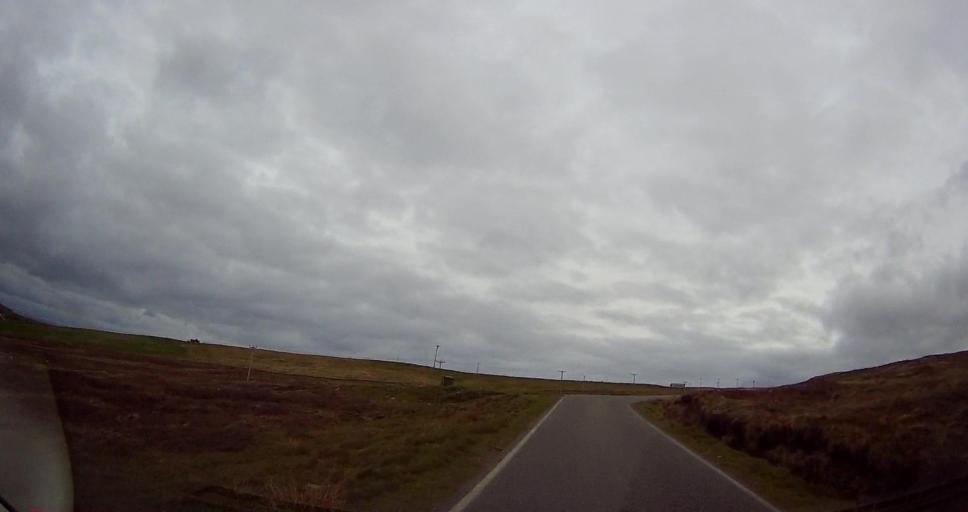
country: GB
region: Scotland
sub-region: Shetland Islands
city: Shetland
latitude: 60.5486
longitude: -1.0619
